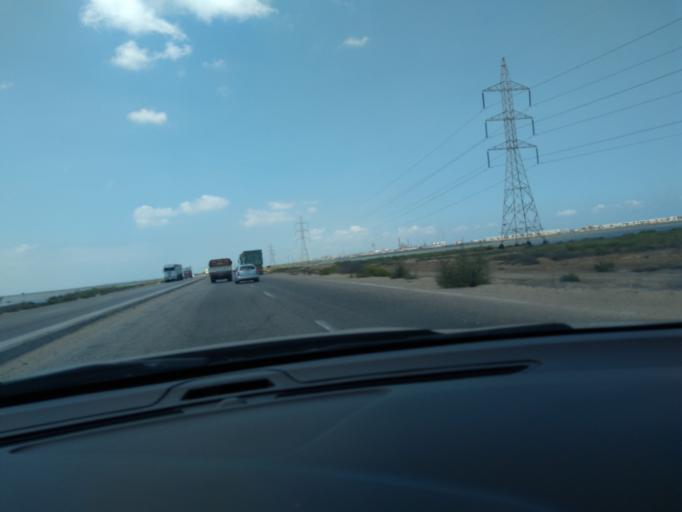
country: EG
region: Muhafazat Bur Sa`id
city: Port Said
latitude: 31.2815
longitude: 32.1887
